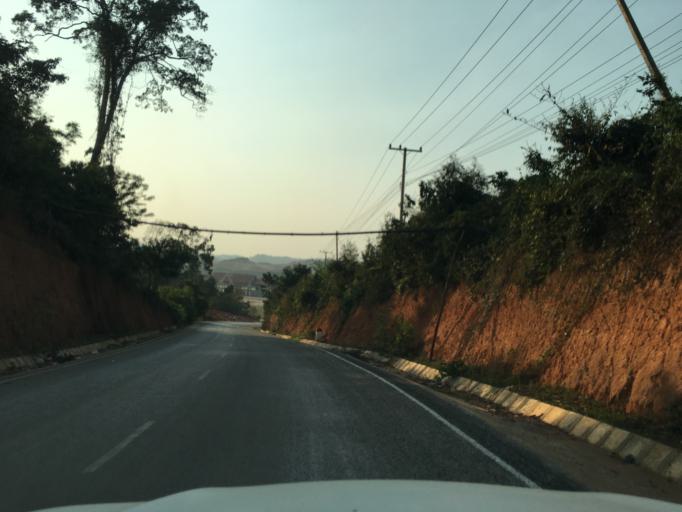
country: LA
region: Houaphan
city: Xam Nua
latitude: 20.6090
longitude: 104.0738
